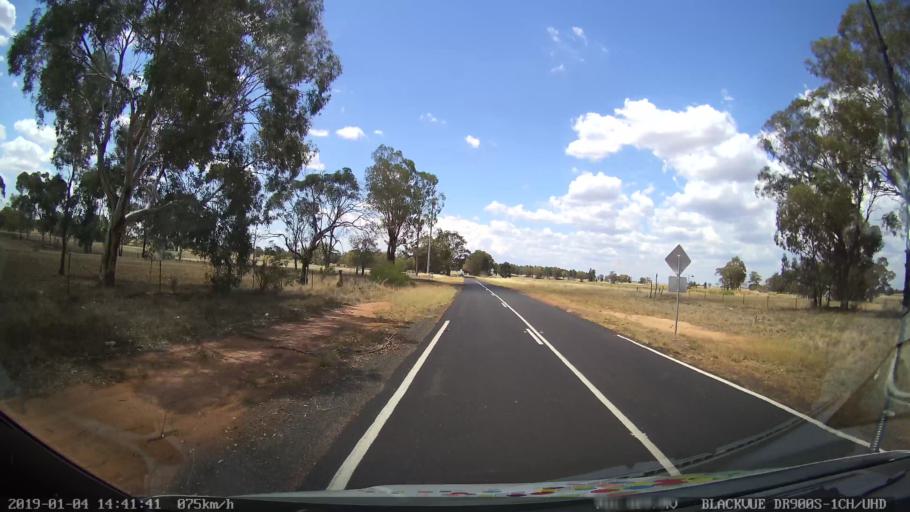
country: AU
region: New South Wales
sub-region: Dubbo Municipality
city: Dubbo
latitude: -32.1363
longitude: 148.6373
